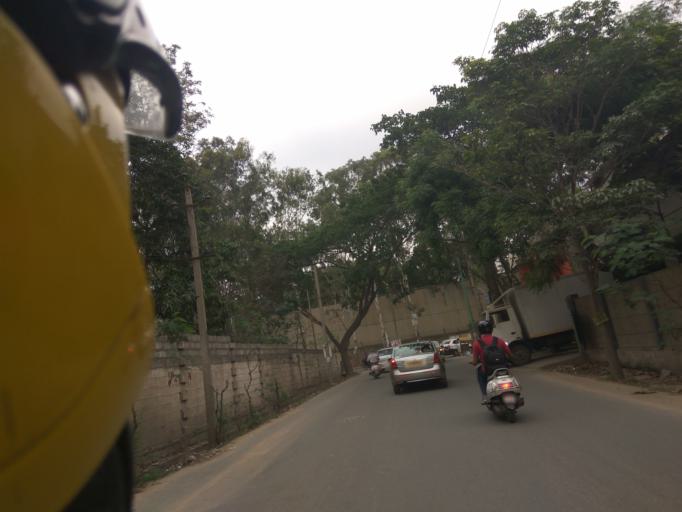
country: IN
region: Karnataka
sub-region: Bangalore Urban
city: Bangalore
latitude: 12.9756
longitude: 77.7078
